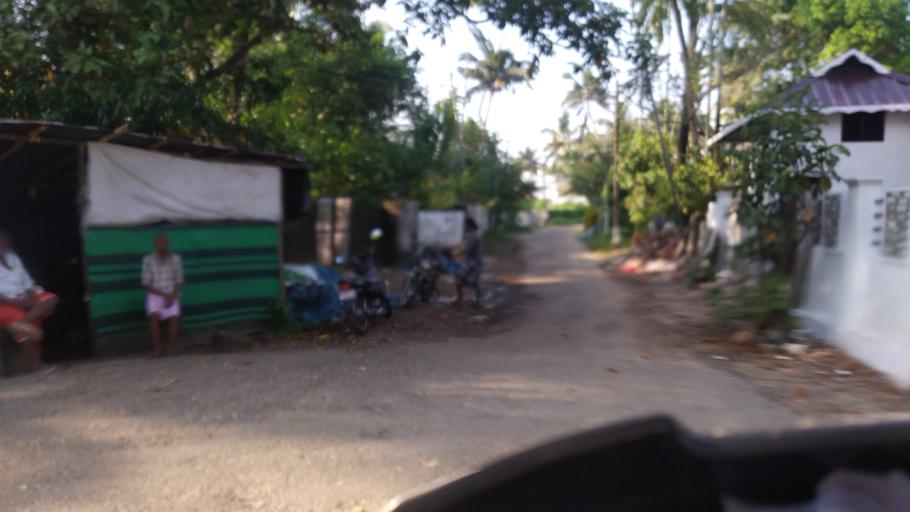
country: IN
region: Kerala
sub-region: Ernakulam
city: Elur
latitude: 10.0388
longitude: 76.2287
